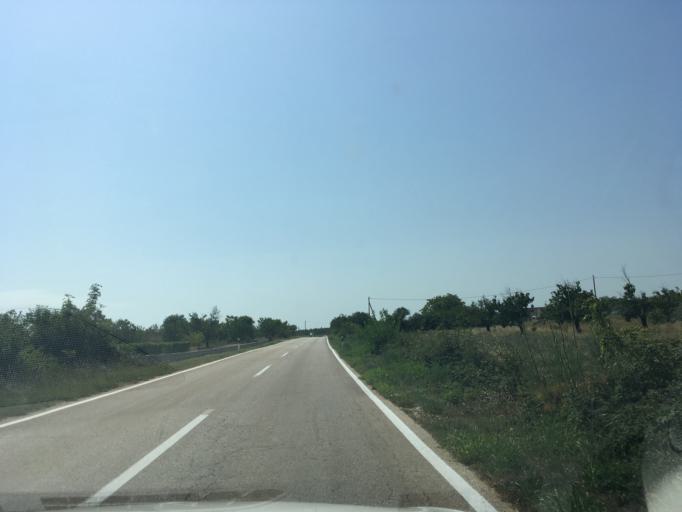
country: HR
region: Zadarska
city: Benkovac
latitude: 43.9643
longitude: 15.7475
